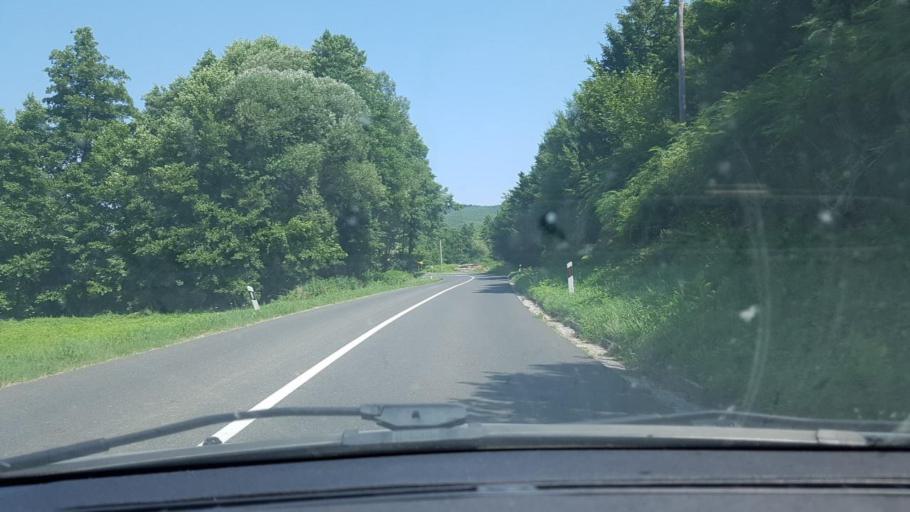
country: BA
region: Federation of Bosnia and Herzegovina
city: Velika Kladusa
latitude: 45.2384
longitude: 15.7364
